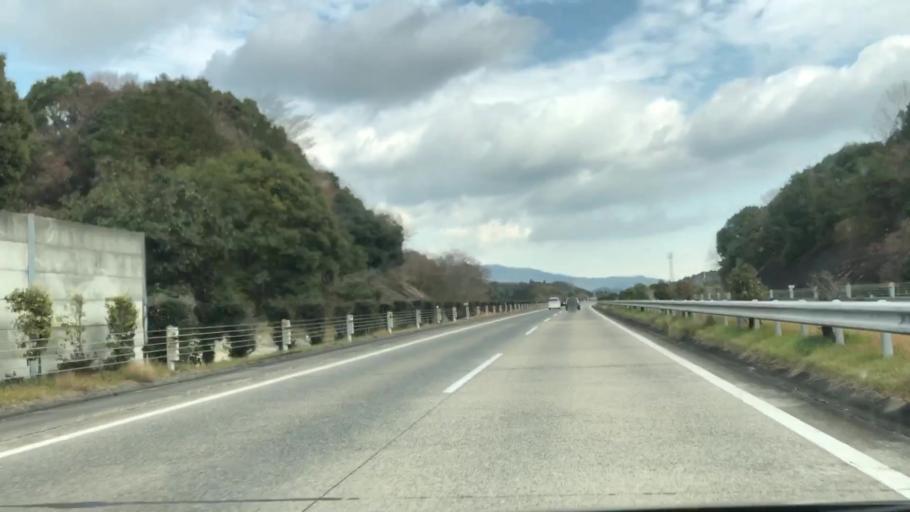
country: JP
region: Saga Prefecture
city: Kanzakimachi-kanzaki
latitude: 33.3492
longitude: 130.3733
